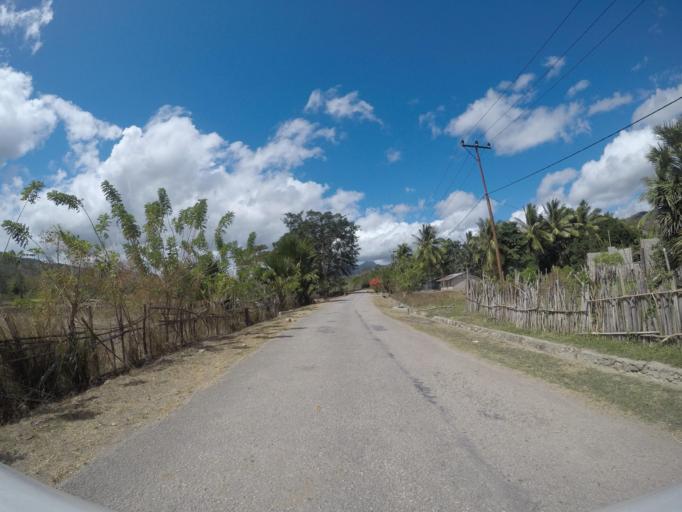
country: TL
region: Lautem
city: Lospalos
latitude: -8.4720
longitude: 126.8173
